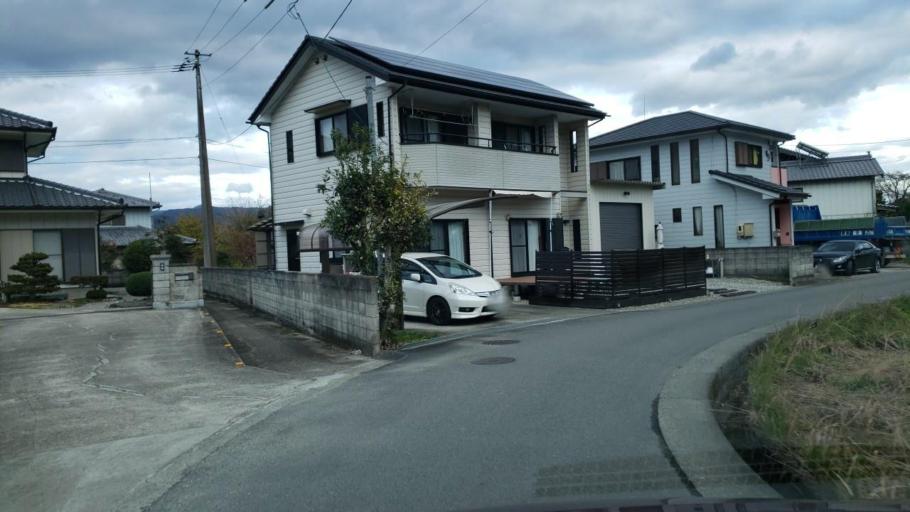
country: JP
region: Tokushima
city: Wakimachi
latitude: 34.0569
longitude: 134.1517
